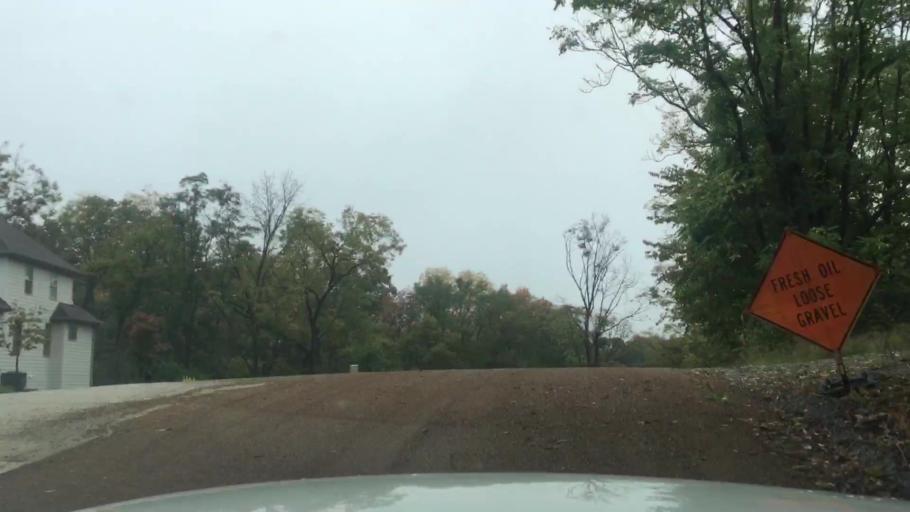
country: US
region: Missouri
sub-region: Boone County
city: Columbia
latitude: 38.8869
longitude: -92.4197
